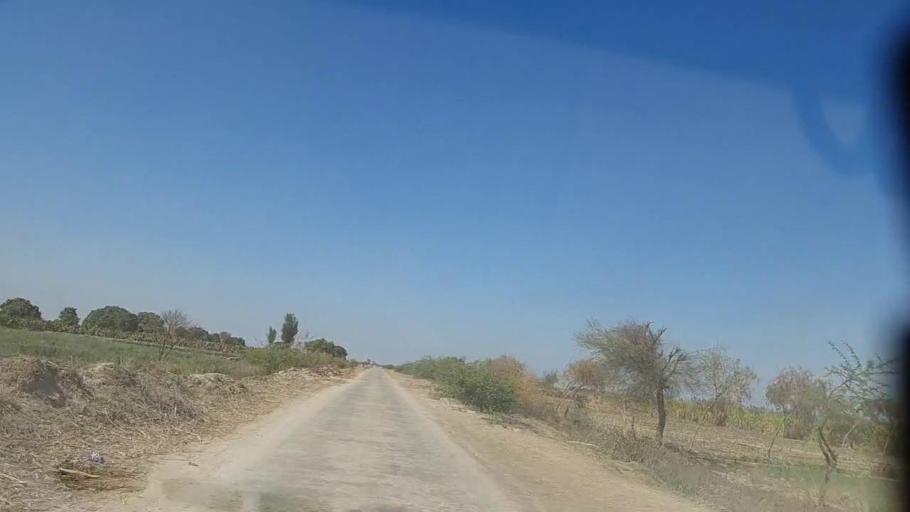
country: PK
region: Sindh
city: Mirwah Gorchani
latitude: 25.2182
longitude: 69.0282
